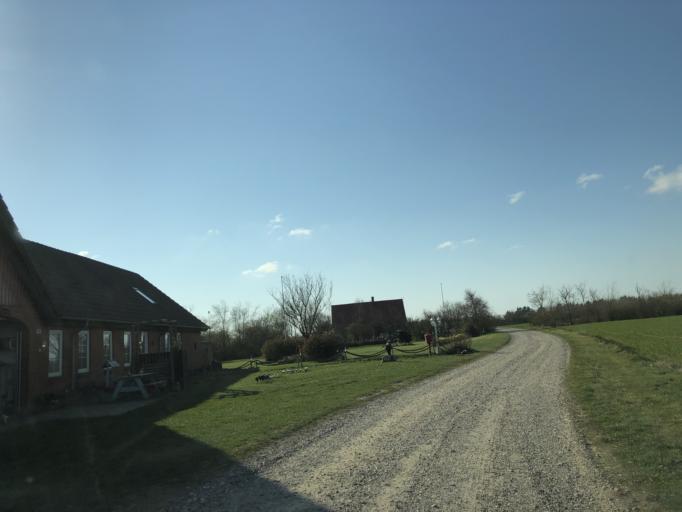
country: DK
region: Central Jutland
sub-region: Holstebro Kommune
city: Ulfborg
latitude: 56.3558
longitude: 8.2528
